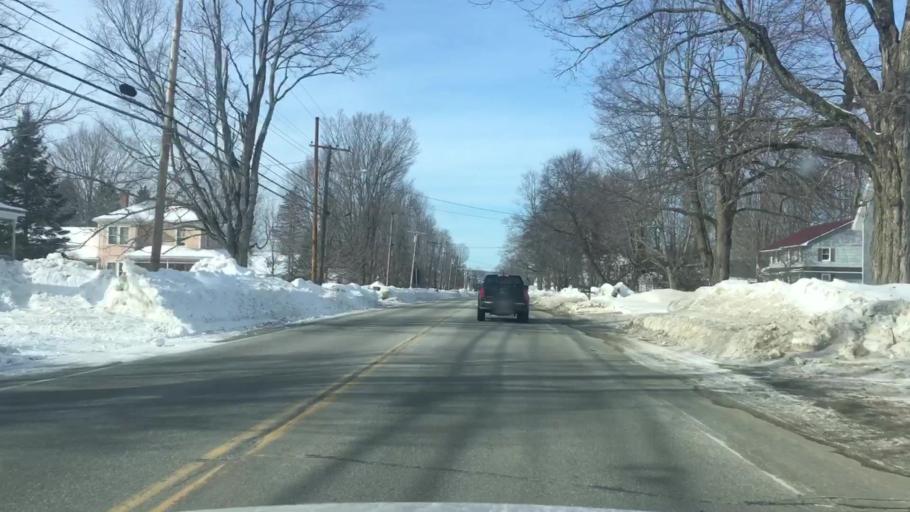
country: US
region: Maine
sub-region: Penobscot County
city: Charleston
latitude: 44.9987
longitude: -69.0211
